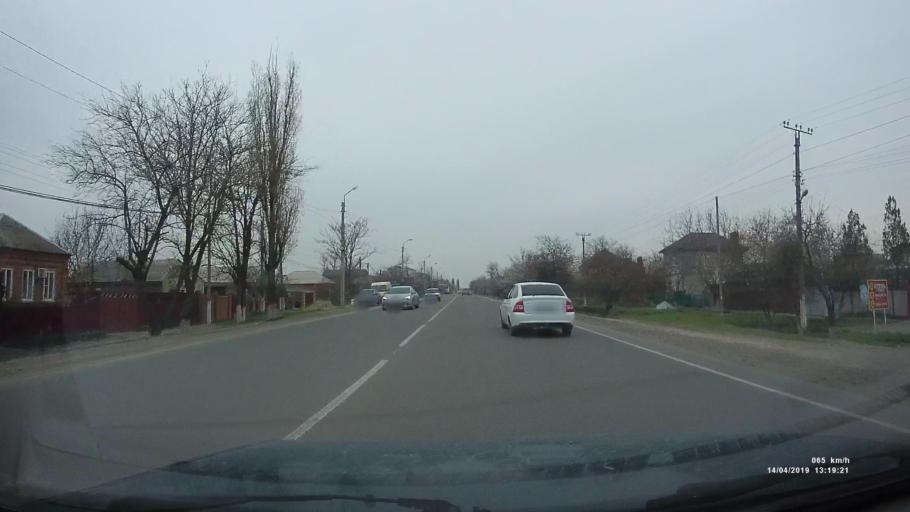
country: RU
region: Rostov
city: Kuleshovka
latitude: 47.0805
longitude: 39.5463
